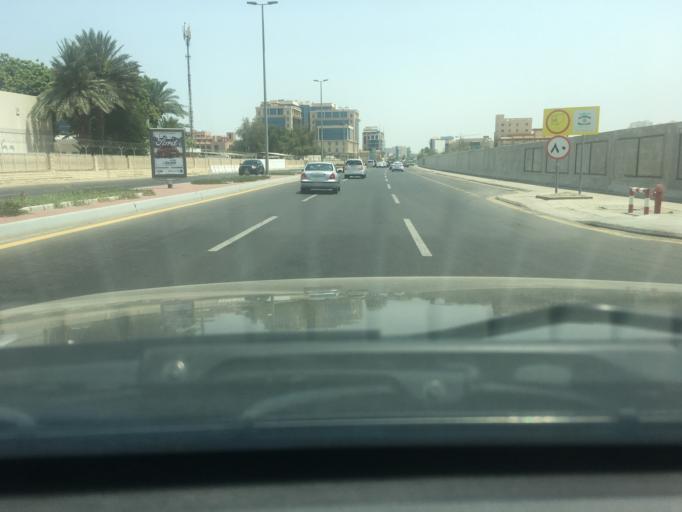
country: SA
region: Makkah
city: Jeddah
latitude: 21.5556
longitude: 39.1429
